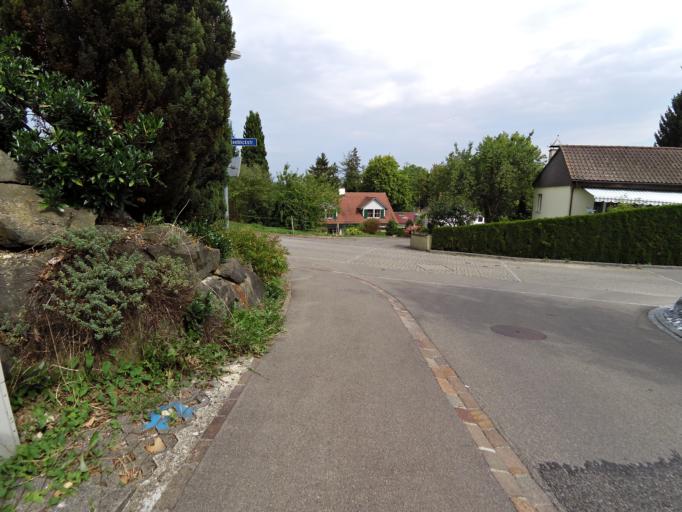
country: CH
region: Thurgau
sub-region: Kreuzlingen District
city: Tagerwilen
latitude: 47.6541
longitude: 9.1264
